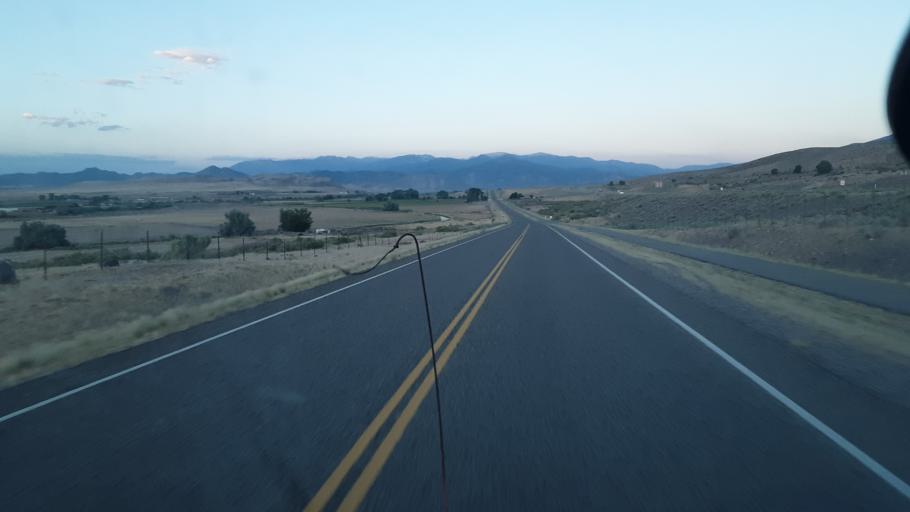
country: US
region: Utah
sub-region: Sevier County
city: Monroe
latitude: 38.6736
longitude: -112.1632
